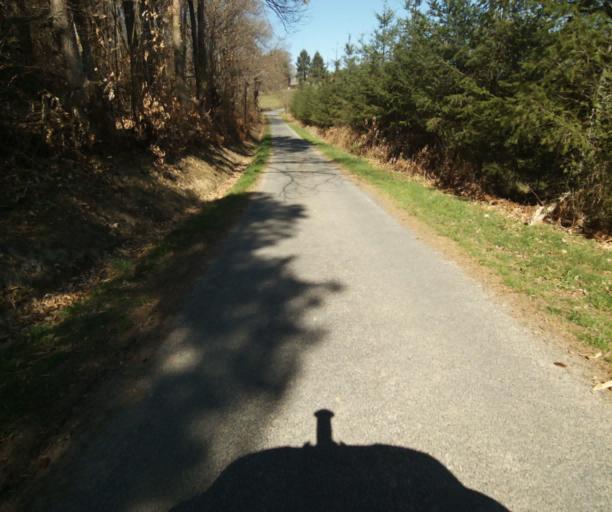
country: FR
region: Limousin
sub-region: Departement de la Correze
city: Saint-Mexant
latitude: 45.2891
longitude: 1.6416
